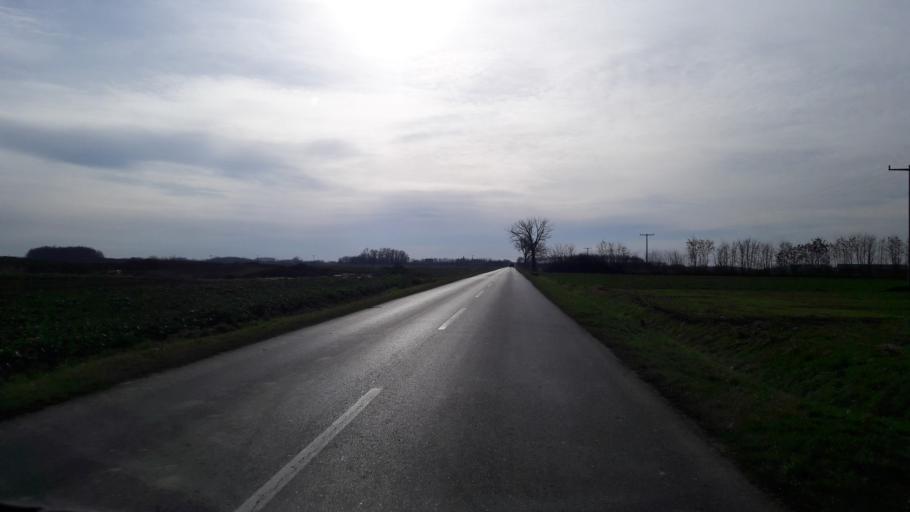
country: HR
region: Osjecko-Baranjska
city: Semeljci
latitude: 45.3235
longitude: 18.5574
